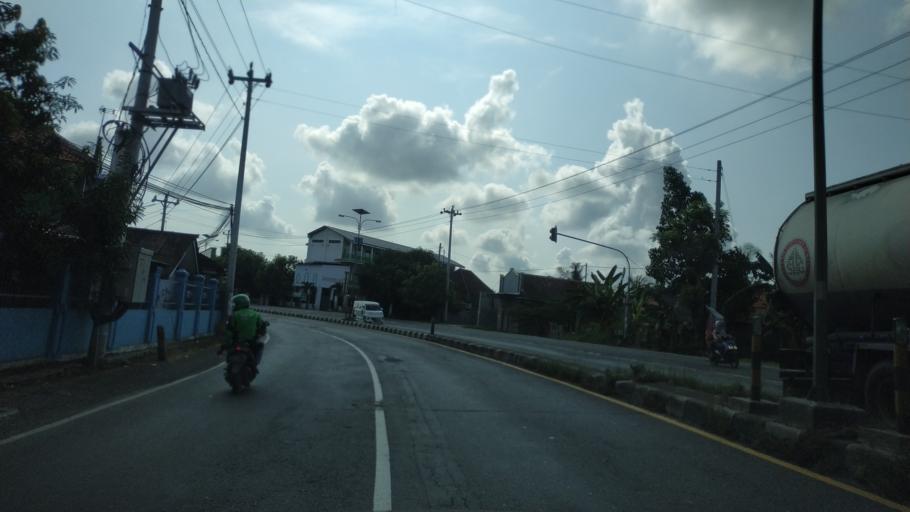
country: ID
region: Central Java
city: Comal
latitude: -6.8977
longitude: 109.5403
